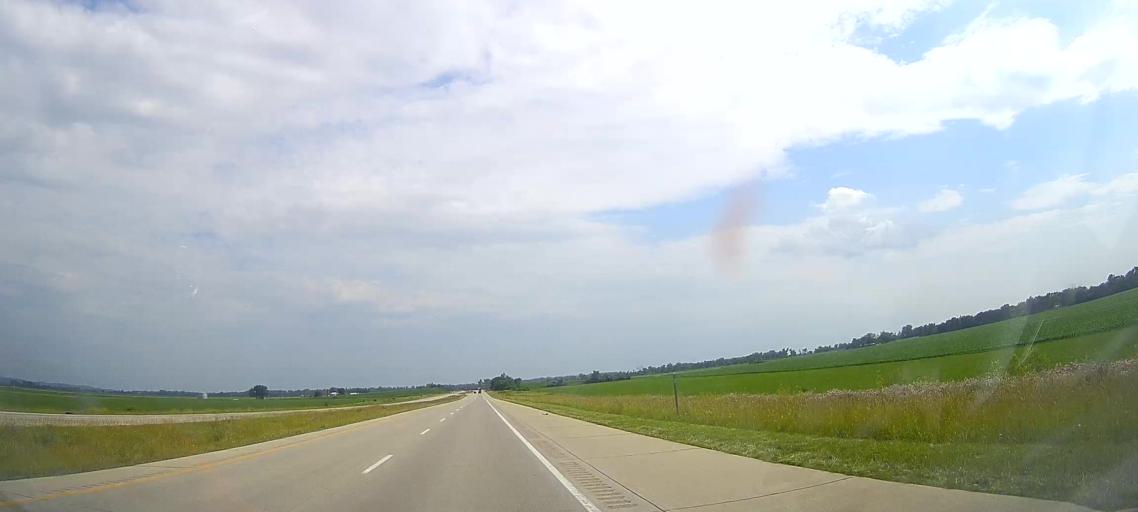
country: US
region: Nebraska
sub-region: Burt County
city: Tekamah
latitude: 41.8640
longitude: -96.1032
